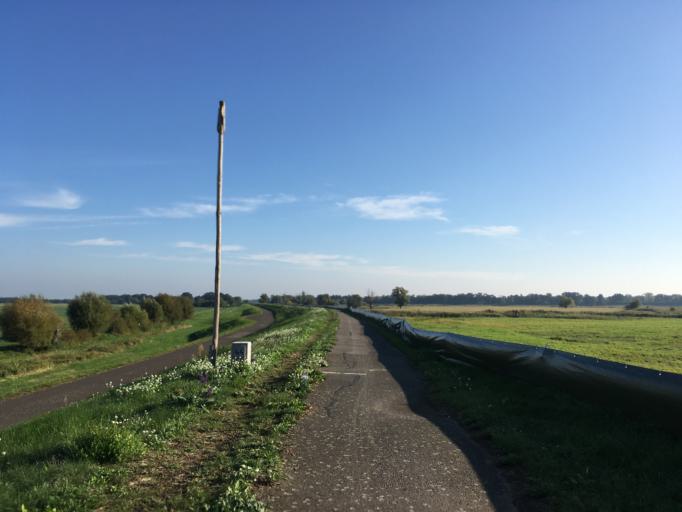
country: DE
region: Brandenburg
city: Reitwein
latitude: 52.4623
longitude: 14.5973
